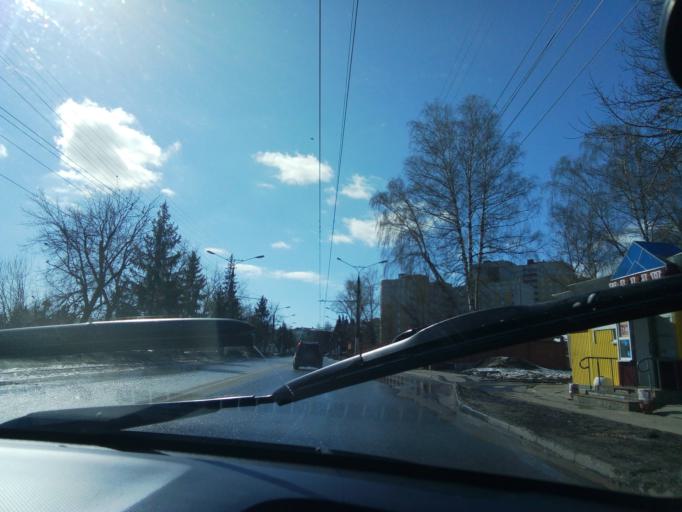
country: RU
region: Chuvashia
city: Novyye Lapsary
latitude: 56.1099
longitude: 47.1804
